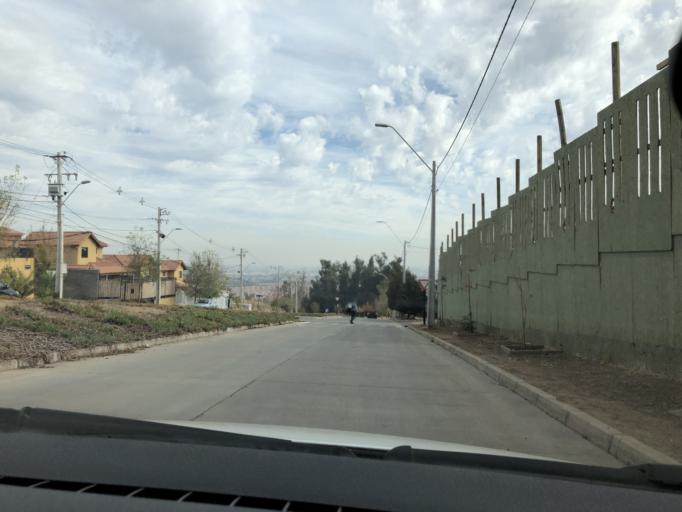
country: CL
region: Santiago Metropolitan
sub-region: Provincia de Cordillera
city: Puente Alto
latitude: -33.5872
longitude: -70.5338
